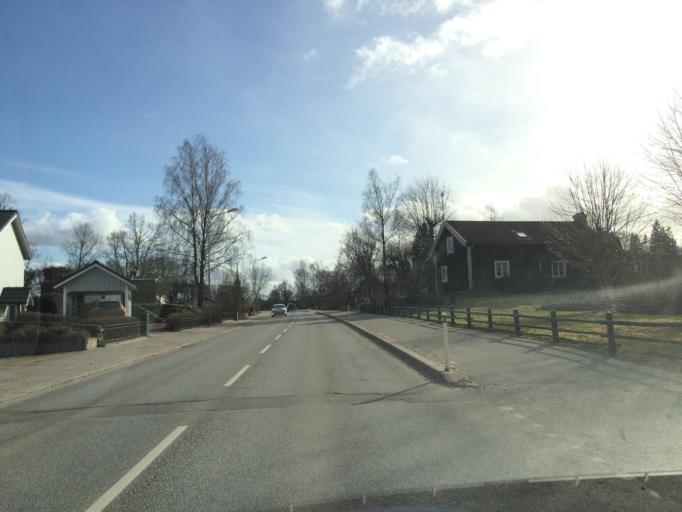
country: SE
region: Kronoberg
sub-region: Almhults Kommun
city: AElmhult
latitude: 56.5575
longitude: 14.1300
